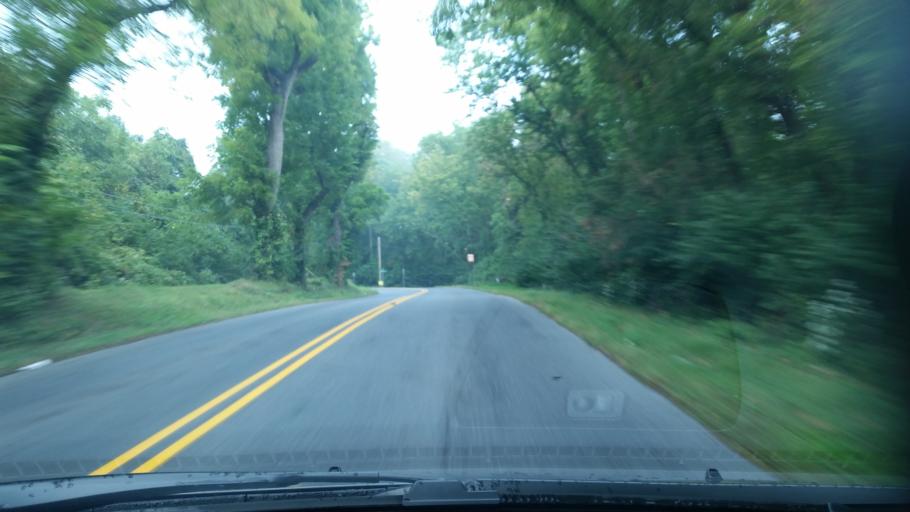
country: US
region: Pennsylvania
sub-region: Lancaster County
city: Lancaster
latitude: 40.0565
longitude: -76.2793
